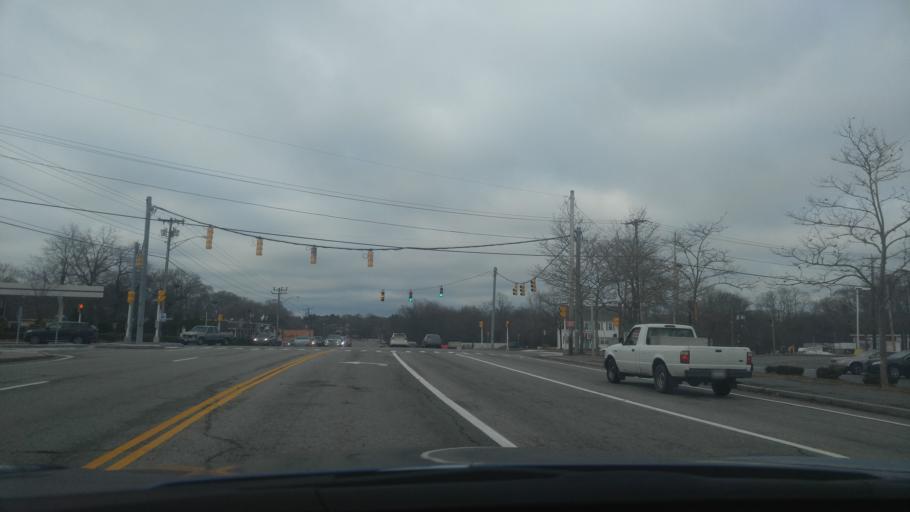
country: US
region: Rhode Island
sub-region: Kent County
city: Warwick
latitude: 41.7120
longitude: -71.3989
